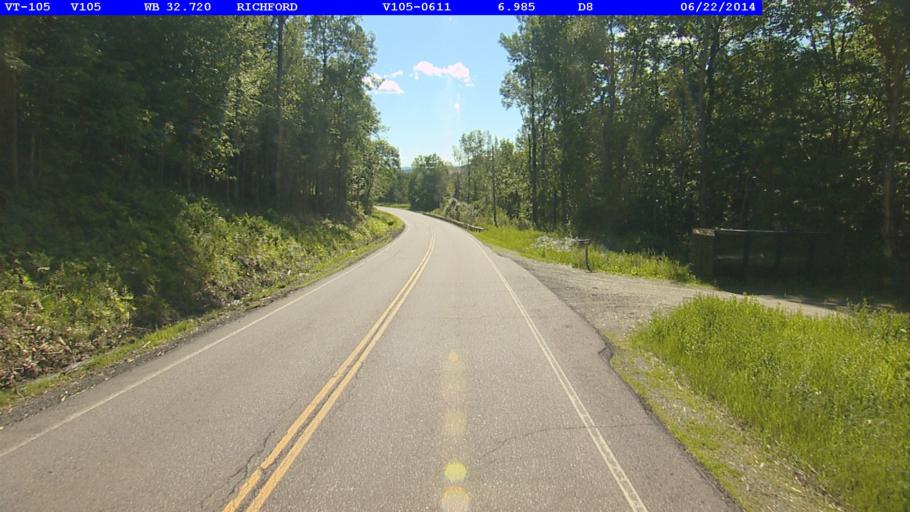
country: US
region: Vermont
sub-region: Franklin County
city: Richford
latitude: 45.0045
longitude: -72.5844
